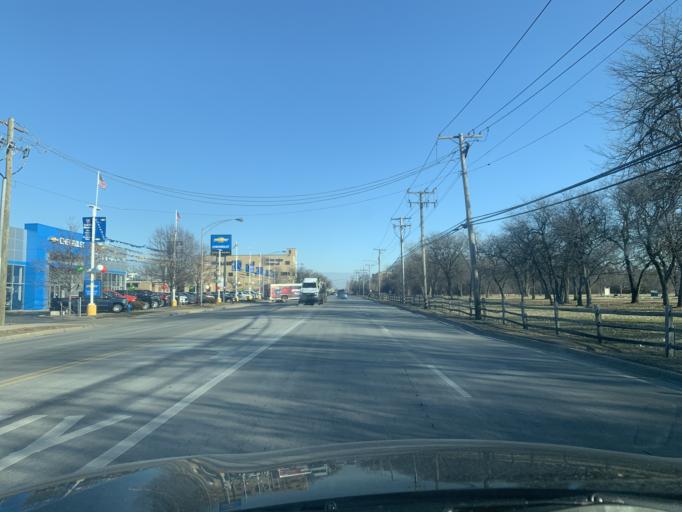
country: US
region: Illinois
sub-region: Cook County
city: Maywood
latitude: 41.8645
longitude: -87.8309
